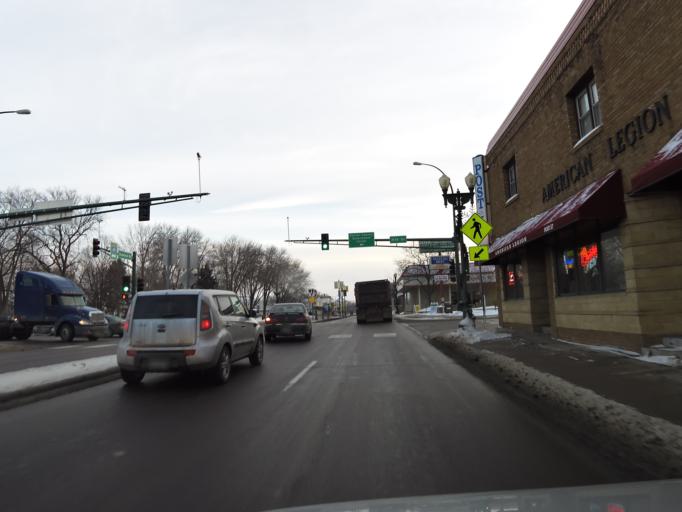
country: US
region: Minnesota
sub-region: Carver County
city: Chaska
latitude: 44.7876
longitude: -93.6013
